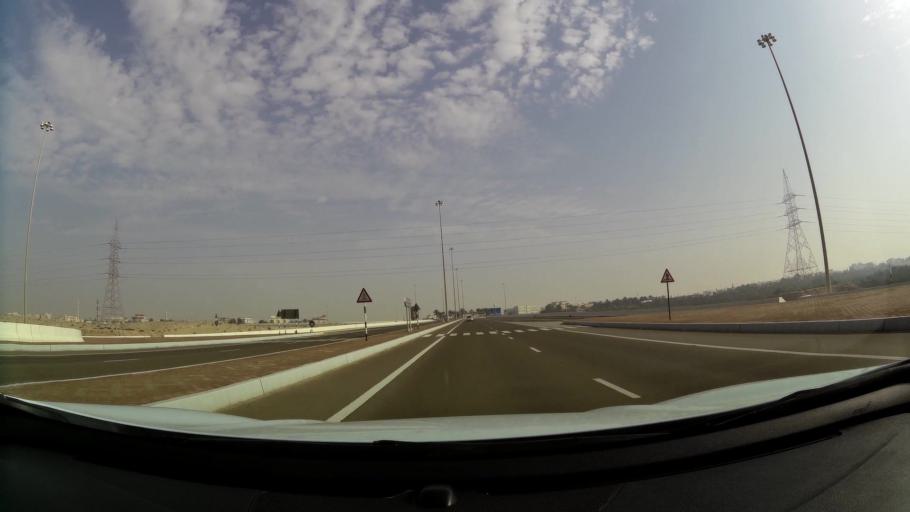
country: AE
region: Abu Dhabi
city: Abu Dhabi
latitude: 24.2528
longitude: 54.7088
